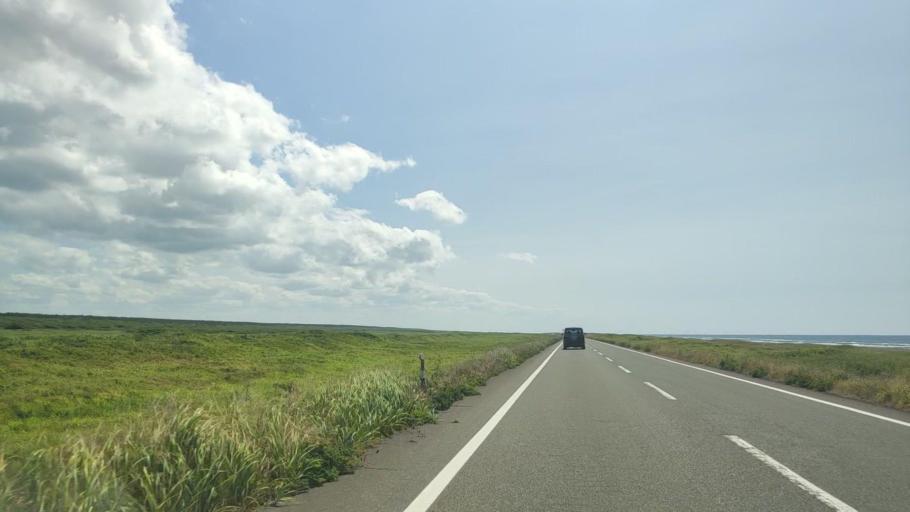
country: JP
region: Hokkaido
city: Wakkanai
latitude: 45.1665
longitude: 141.5833
